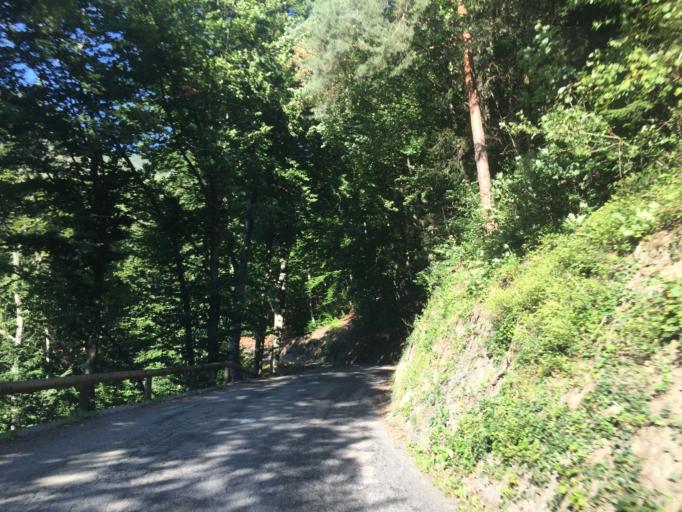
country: FR
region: Rhone-Alpes
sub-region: Departement de la Savoie
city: Moutiers
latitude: 45.5076
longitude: 6.5722
